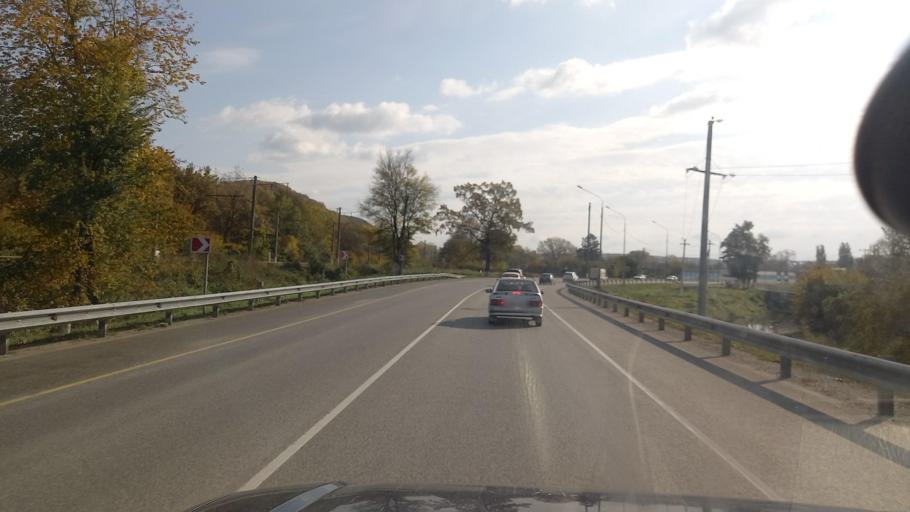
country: RU
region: Krasnodarskiy
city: Krymsk
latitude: 44.8713
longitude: 37.8413
